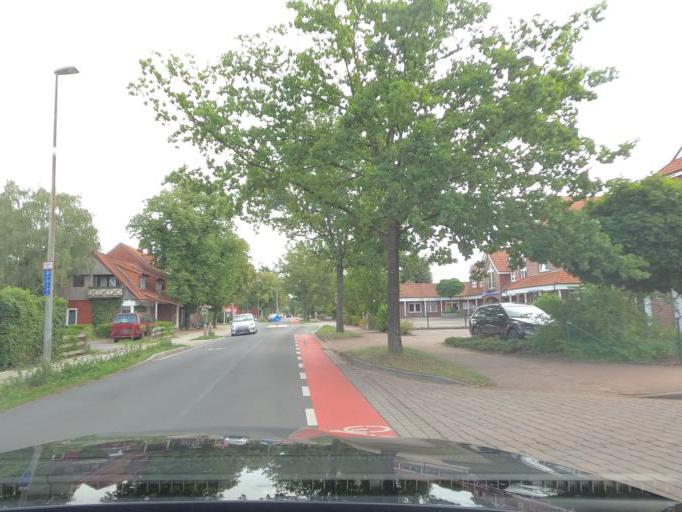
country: DE
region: Lower Saxony
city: Isernhagen Farster Bauerschaft
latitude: 52.5127
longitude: 9.9143
